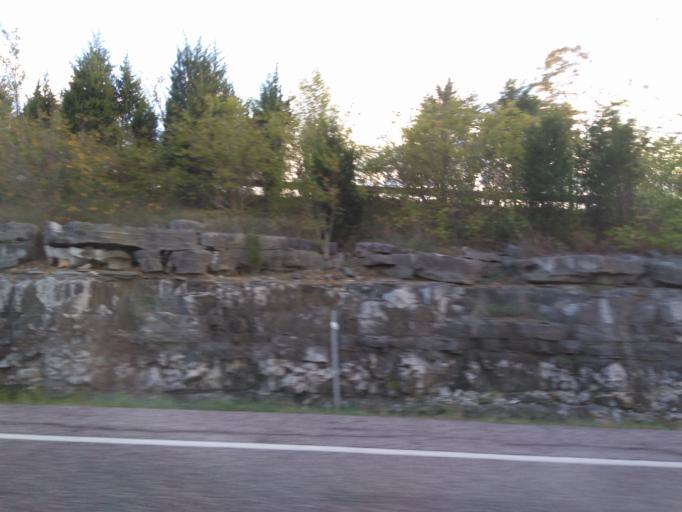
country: US
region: Missouri
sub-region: Saint Louis County
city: Sunset Hills
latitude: 38.5242
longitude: -90.3983
